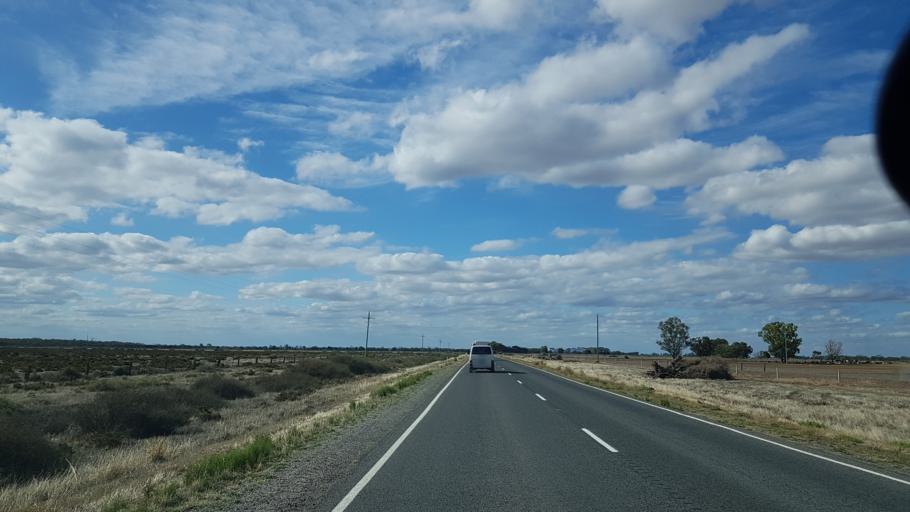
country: AU
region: Victoria
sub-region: Swan Hill
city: Swan Hill
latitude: -35.8363
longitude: 143.9416
